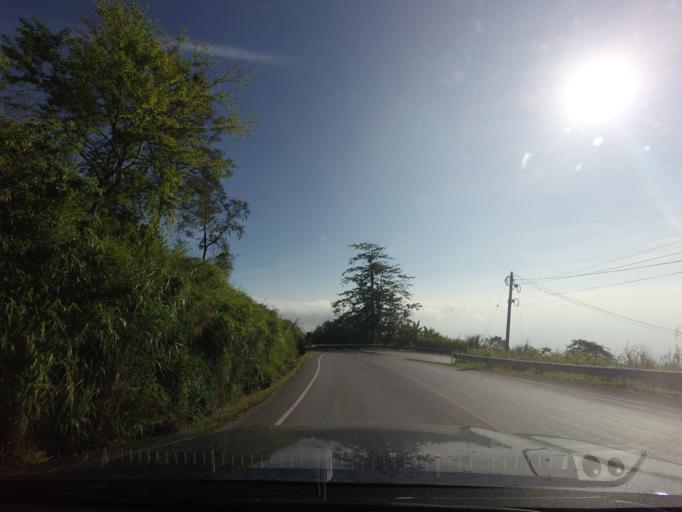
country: TH
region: Phetchabun
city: Lom Kao
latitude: 16.8796
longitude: 101.1025
